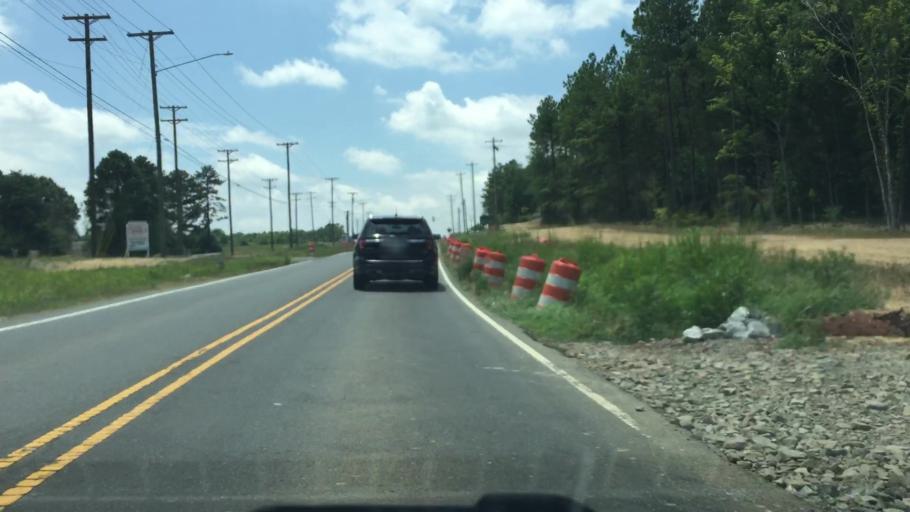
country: US
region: North Carolina
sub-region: Cabarrus County
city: Harrisburg
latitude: 35.3817
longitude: -80.7227
